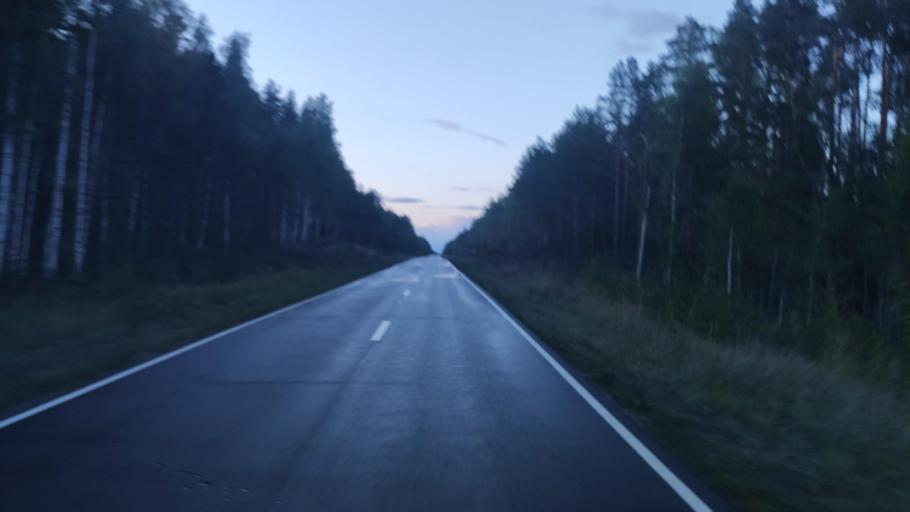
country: RU
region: Vladimir
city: Galitsy
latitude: 56.0711
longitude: 42.8670
